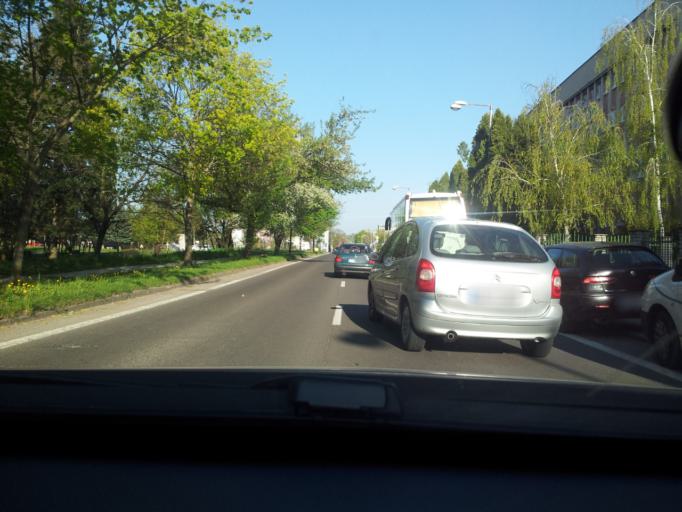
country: SK
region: Nitriansky
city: Zlate Moravce
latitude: 48.3825
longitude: 18.3913
